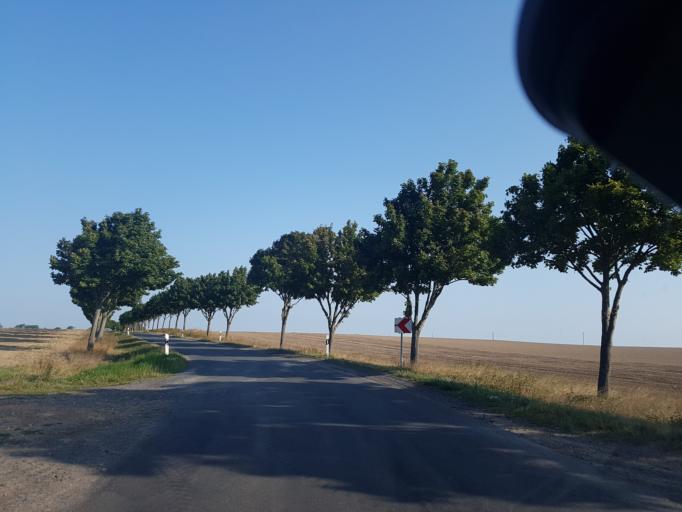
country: DE
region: Brandenburg
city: Niemegk
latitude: 52.0155
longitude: 12.6885
